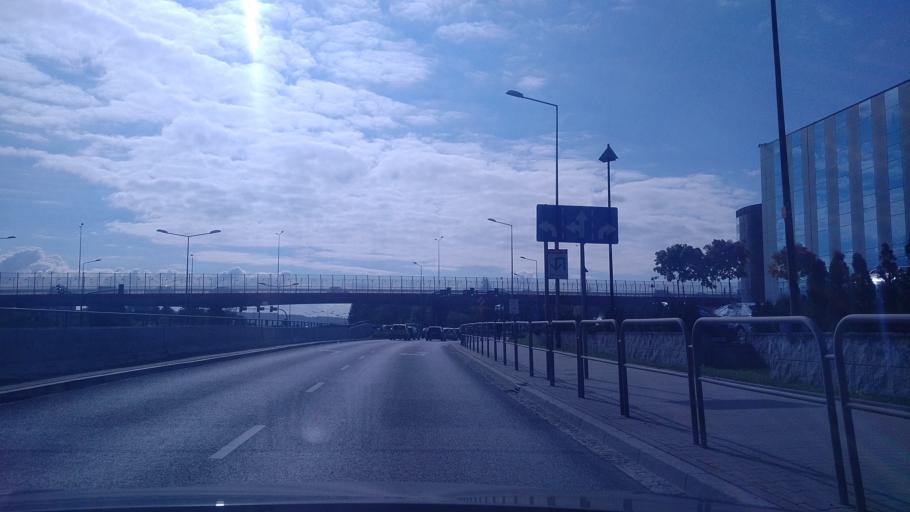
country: PL
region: Lesser Poland Voivodeship
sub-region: Powiat krakowski
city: Zielonki
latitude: 50.0887
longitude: 19.8922
